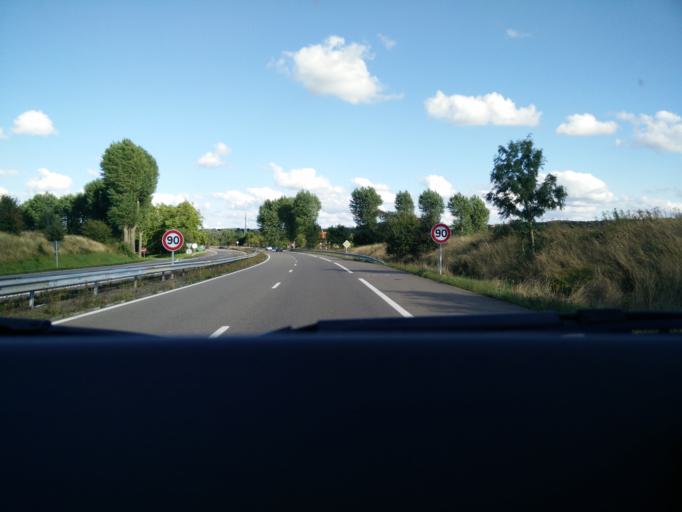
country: FR
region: Nord-Pas-de-Calais
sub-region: Departement du Nord
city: Marpent
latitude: 50.2944
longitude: 4.0655
